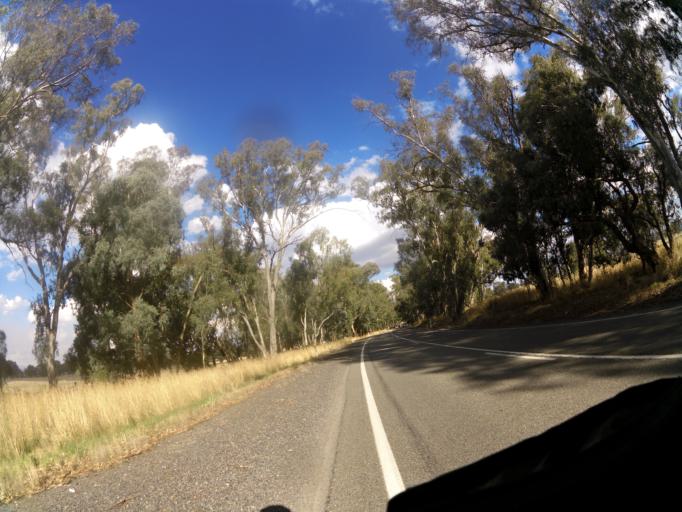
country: AU
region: Victoria
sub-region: Mansfield
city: Mansfield
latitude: -37.0040
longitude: 146.0787
